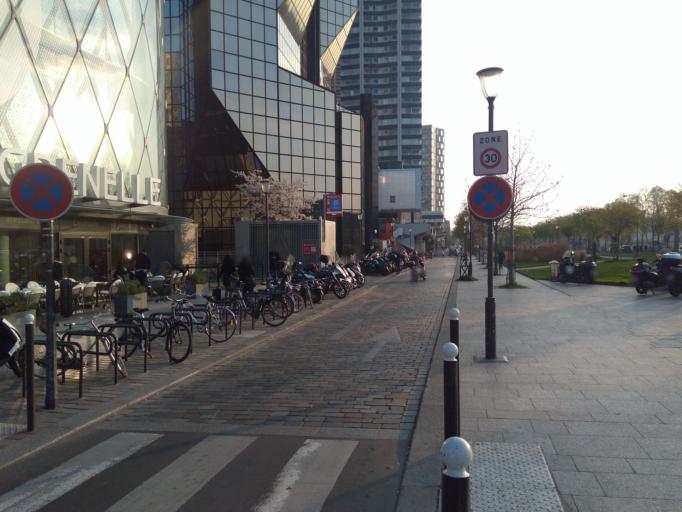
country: FR
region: Ile-de-France
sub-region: Departement des Hauts-de-Seine
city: Vanves
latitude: 48.8487
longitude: 2.2824
